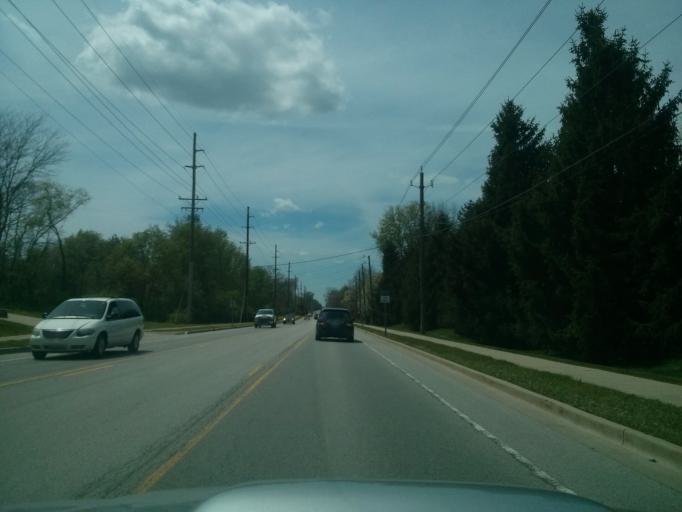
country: US
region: Indiana
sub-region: Hamilton County
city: Carmel
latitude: 39.9567
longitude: -86.0785
